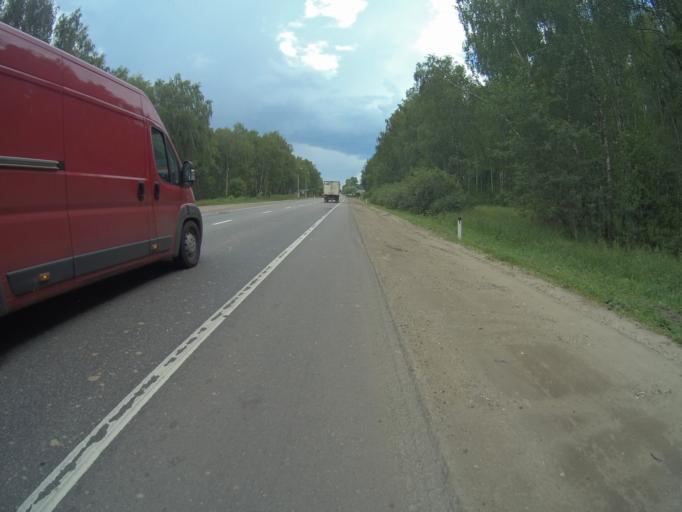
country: RU
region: Vladimir
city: Orgtrud
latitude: 56.2098
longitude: 40.6501
